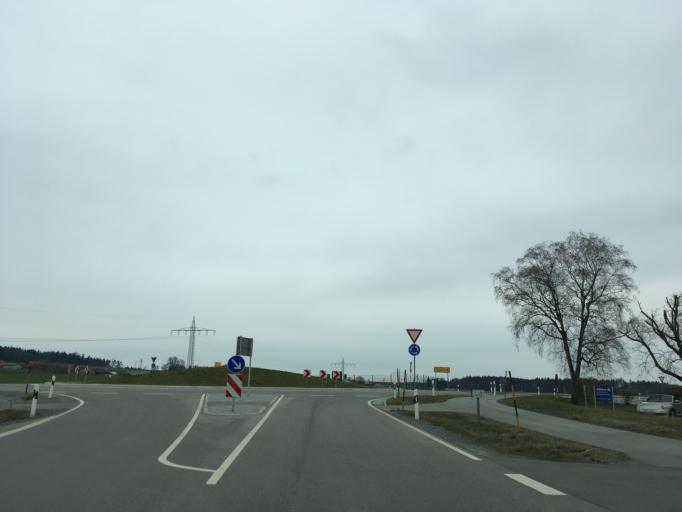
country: DE
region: Bavaria
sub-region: Upper Bavaria
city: Schnaitsee
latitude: 48.0686
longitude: 12.3884
